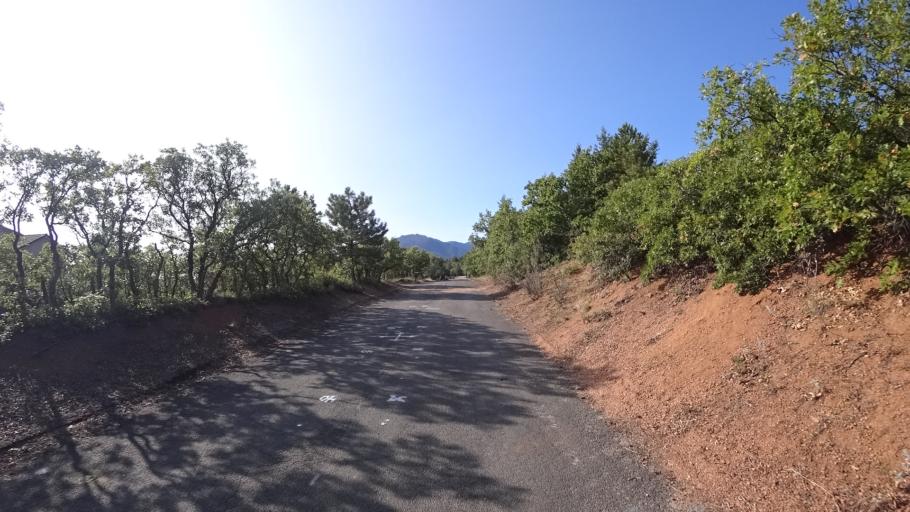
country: US
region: Colorado
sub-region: El Paso County
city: Colorado Springs
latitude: 38.8089
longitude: -104.8733
